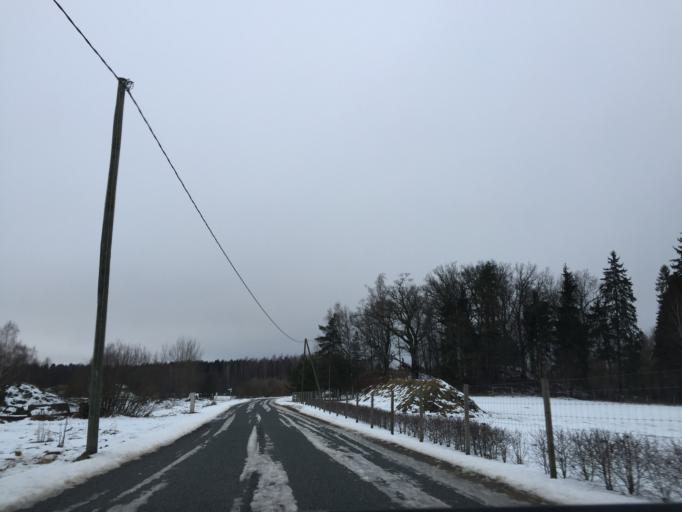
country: LV
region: Krimulda
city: Ragana
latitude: 57.1842
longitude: 24.6957
